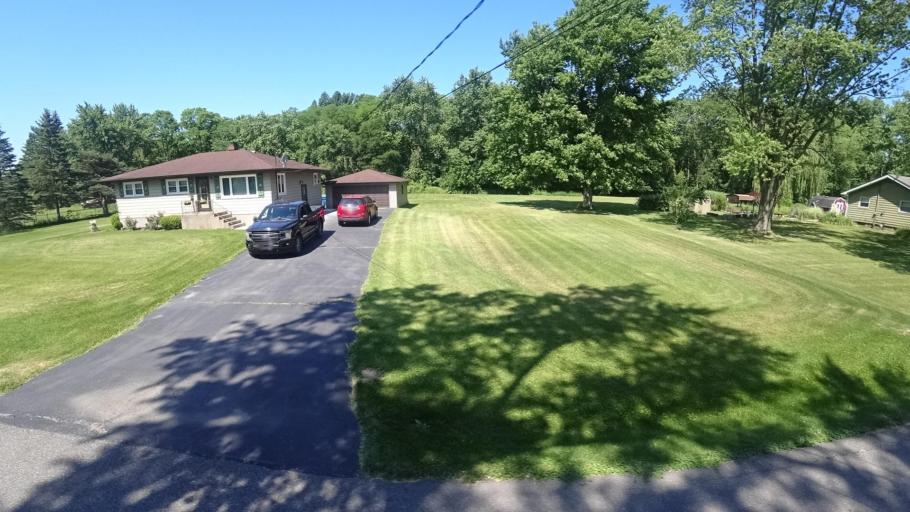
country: US
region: Indiana
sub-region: Porter County
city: Burns Harbor
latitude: 41.6125
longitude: -87.1182
